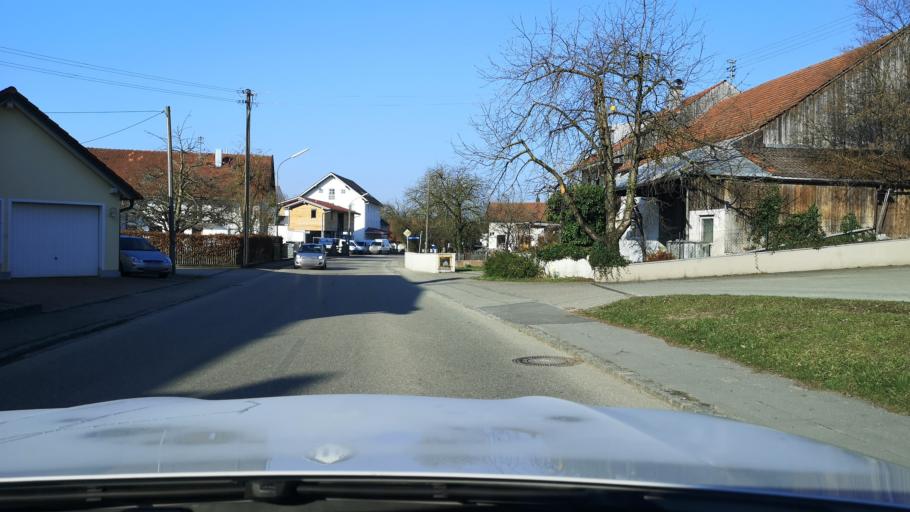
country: DE
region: Bavaria
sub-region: Upper Bavaria
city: Finsing
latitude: 48.2160
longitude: 11.8270
